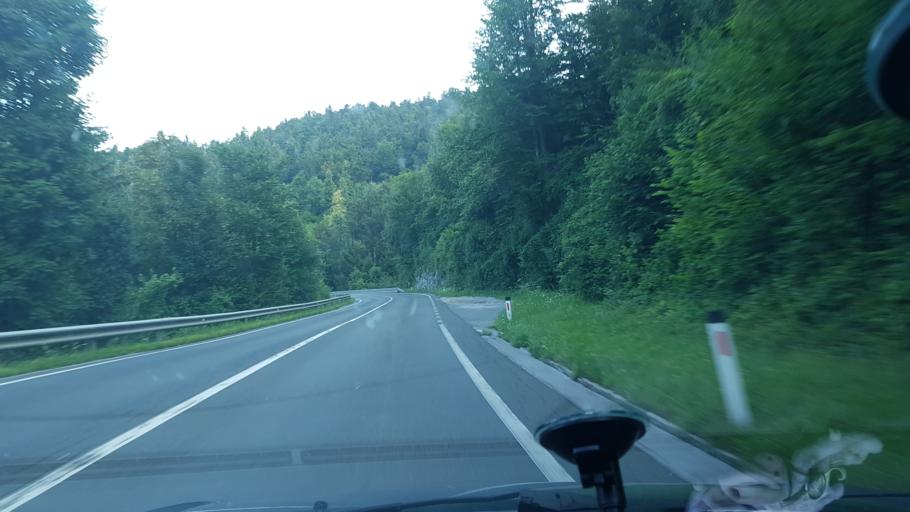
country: SI
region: Vrhnika
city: Vrhnika
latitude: 45.9525
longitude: 14.2568
